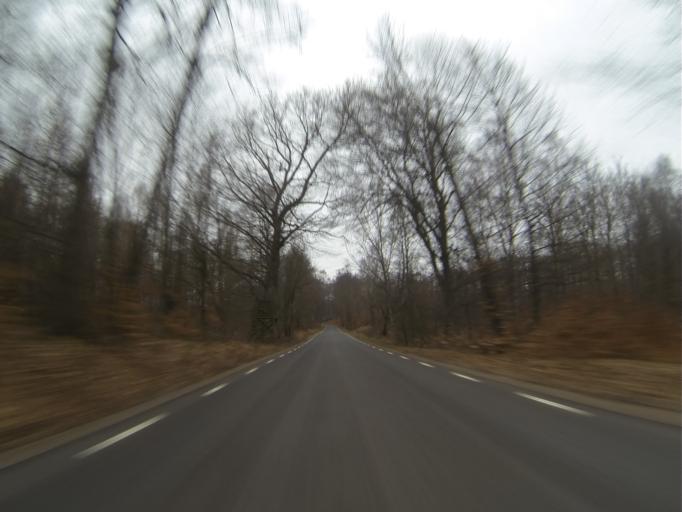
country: SE
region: Skane
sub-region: Lunds Kommun
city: Genarp
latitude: 55.5602
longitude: 13.4331
